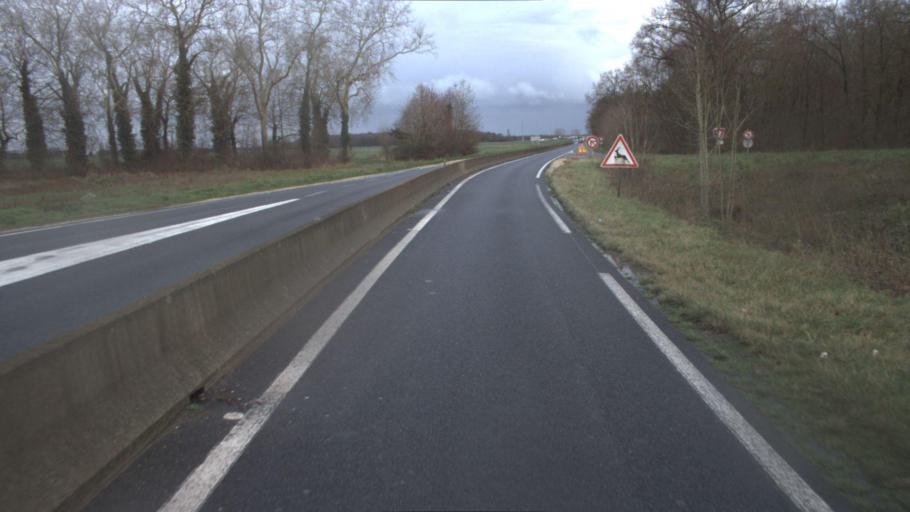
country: FR
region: Ile-de-France
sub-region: Departement de l'Essonne
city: Le Coudray-Montceaux
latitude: 48.5542
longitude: 2.5039
